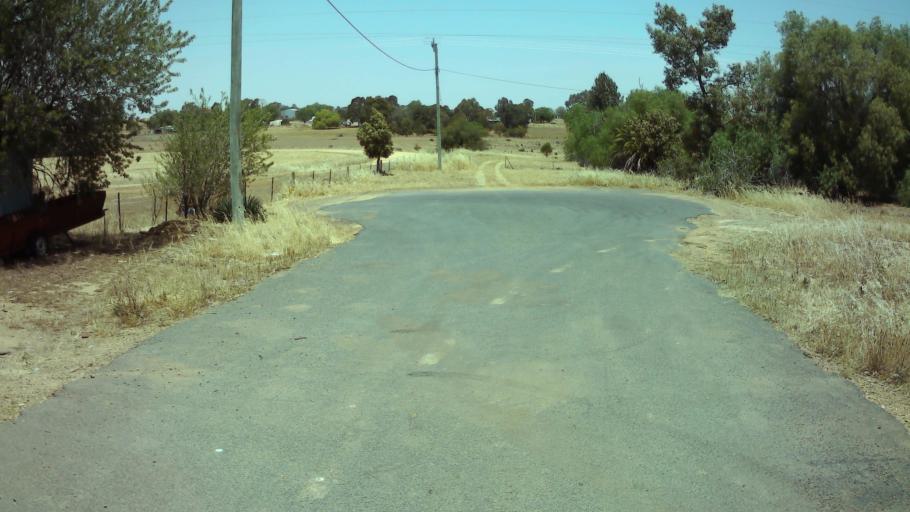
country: AU
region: New South Wales
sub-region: Weddin
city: Grenfell
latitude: -33.8977
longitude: 148.1708
